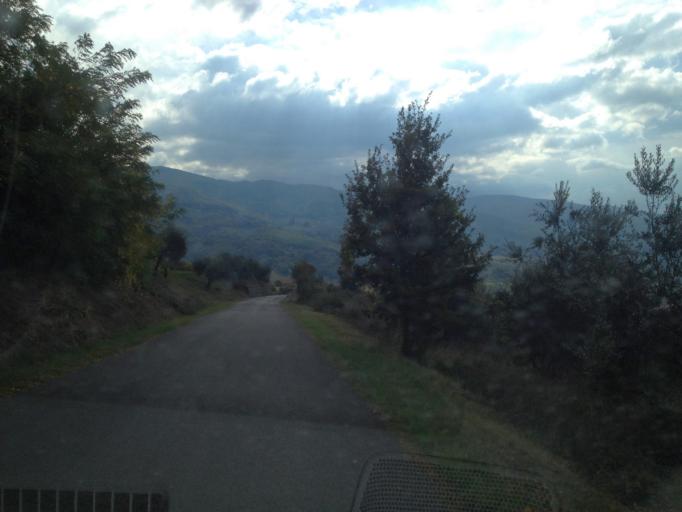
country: IT
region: Tuscany
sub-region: Province of Florence
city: Montebonello
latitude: 43.8581
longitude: 11.4984
